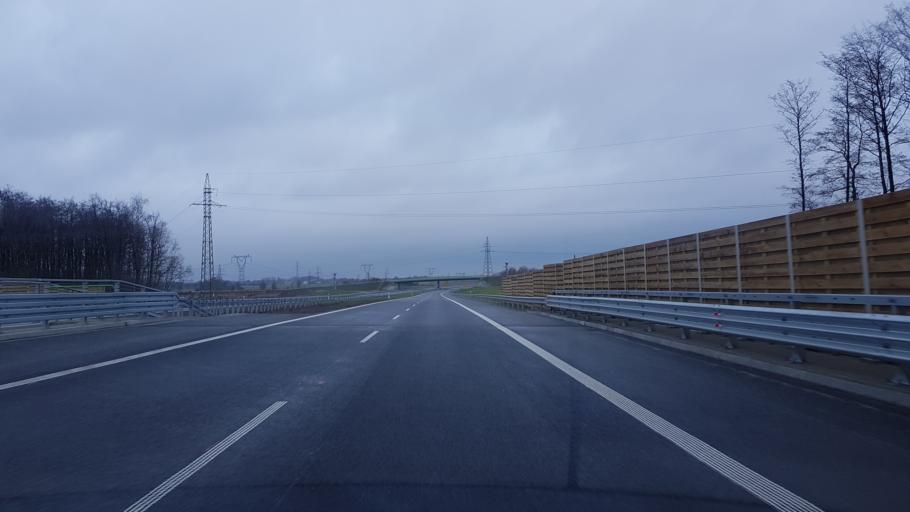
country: PL
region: West Pomeranian Voivodeship
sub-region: Koszalin
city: Koszalin
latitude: 54.2197
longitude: 16.1604
